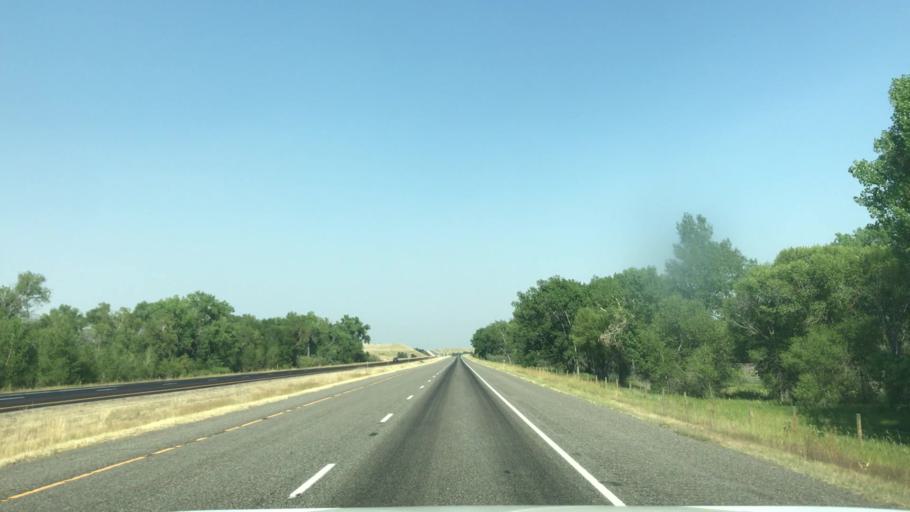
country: US
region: Montana
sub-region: Cascade County
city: Sun Prairie
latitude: 47.2347
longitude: -111.7456
